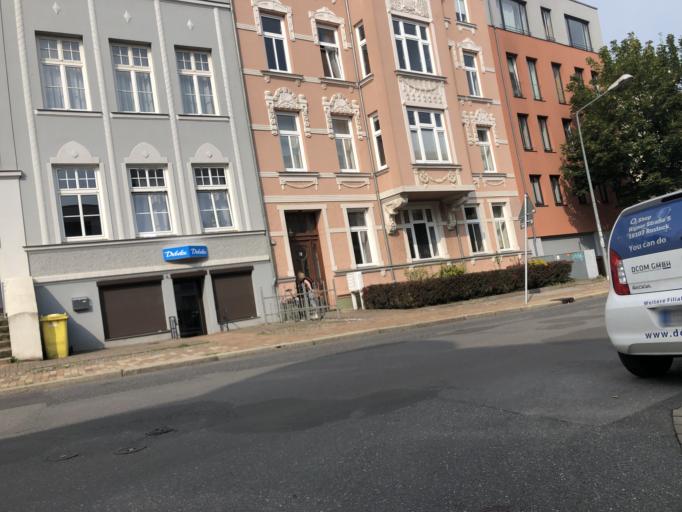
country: DE
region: Mecklenburg-Vorpommern
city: Rostock
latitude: 54.0801
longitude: 12.1432
